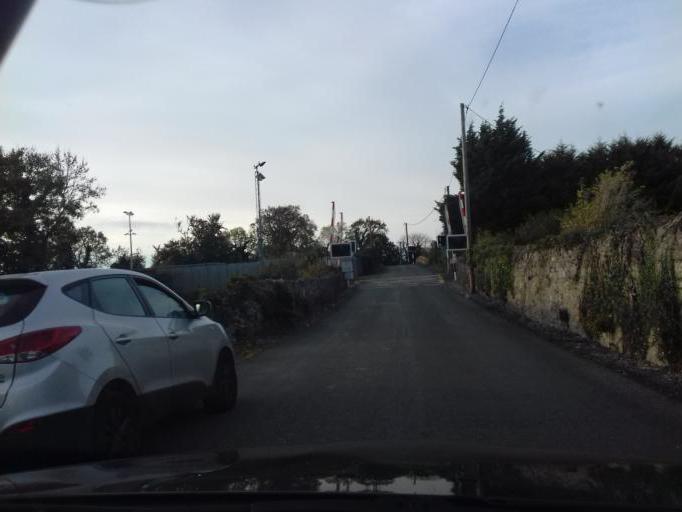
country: IE
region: Leinster
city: Hartstown
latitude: 53.3833
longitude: -6.4394
